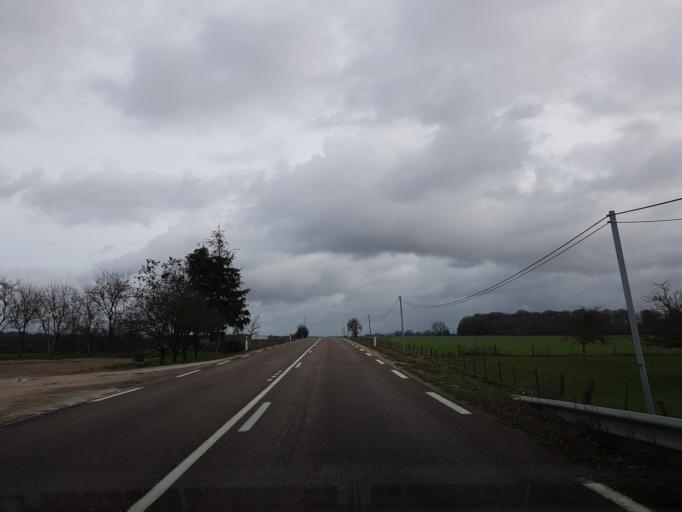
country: FR
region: Champagne-Ardenne
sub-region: Departement de la Haute-Marne
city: Fayl-Billot
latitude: 47.7706
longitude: 5.6970
